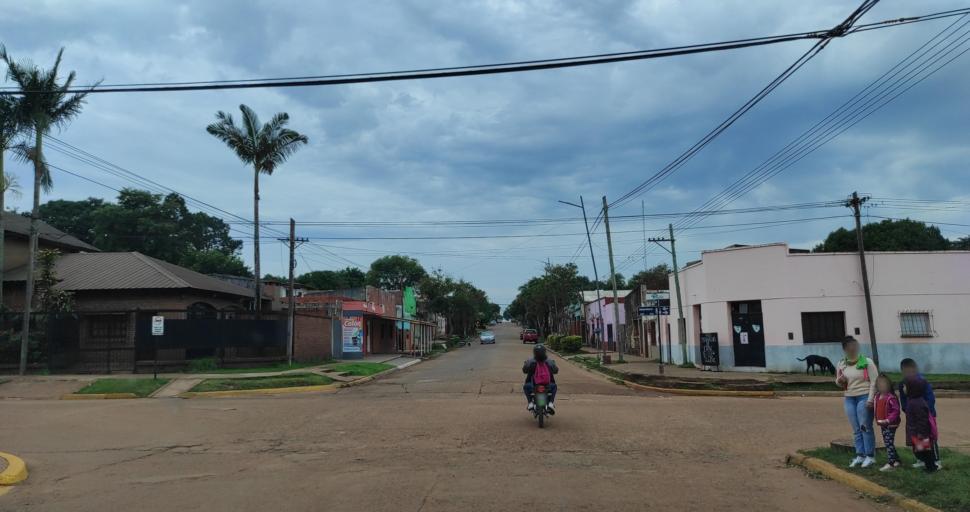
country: AR
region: Corrientes
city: Santo Tome
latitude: -28.5523
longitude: -56.0454
